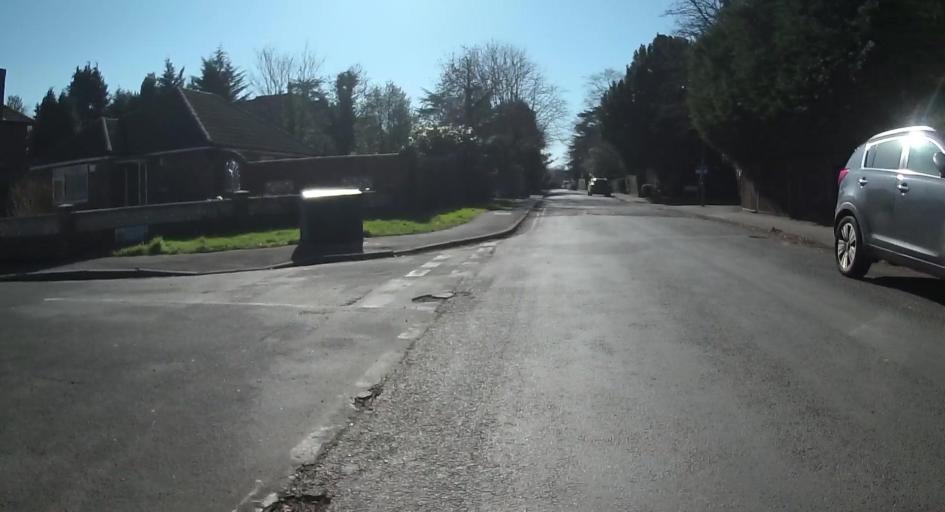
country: GB
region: England
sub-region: Surrey
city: Addlestone
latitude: 51.3705
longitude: -0.4857
